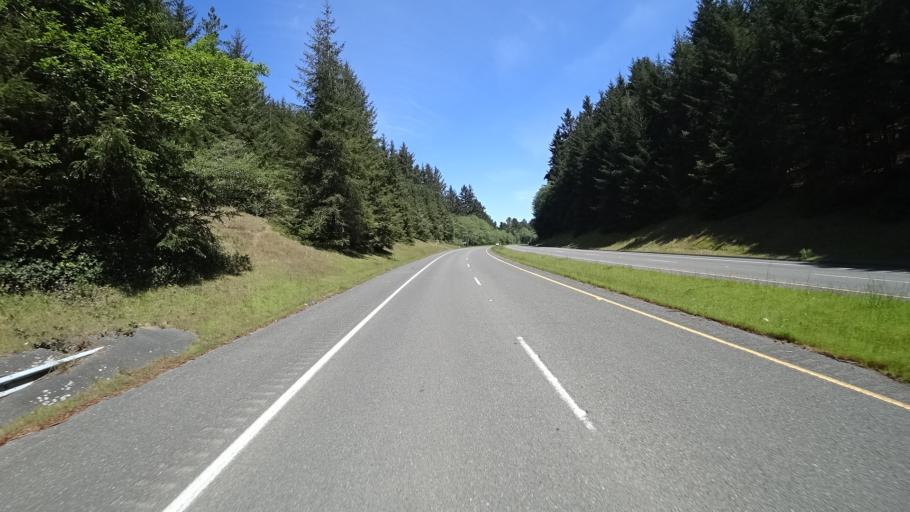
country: US
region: California
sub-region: Humboldt County
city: Westhaven-Moonstone
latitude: 41.1317
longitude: -124.1505
